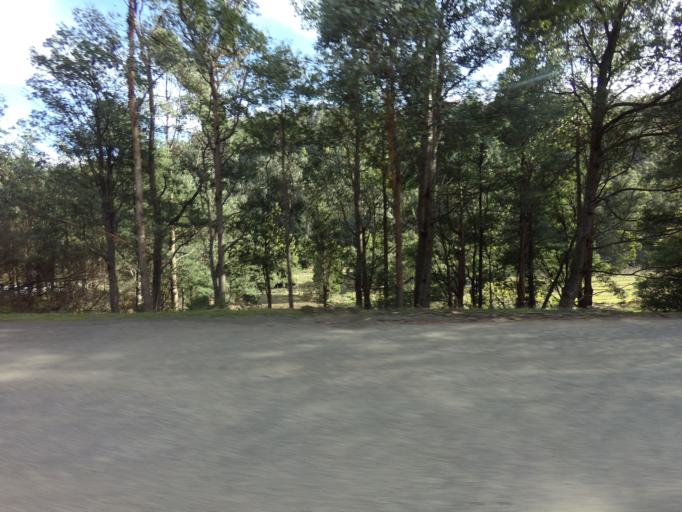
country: AU
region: Tasmania
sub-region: Huon Valley
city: Huonville
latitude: -43.0378
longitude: 147.1388
